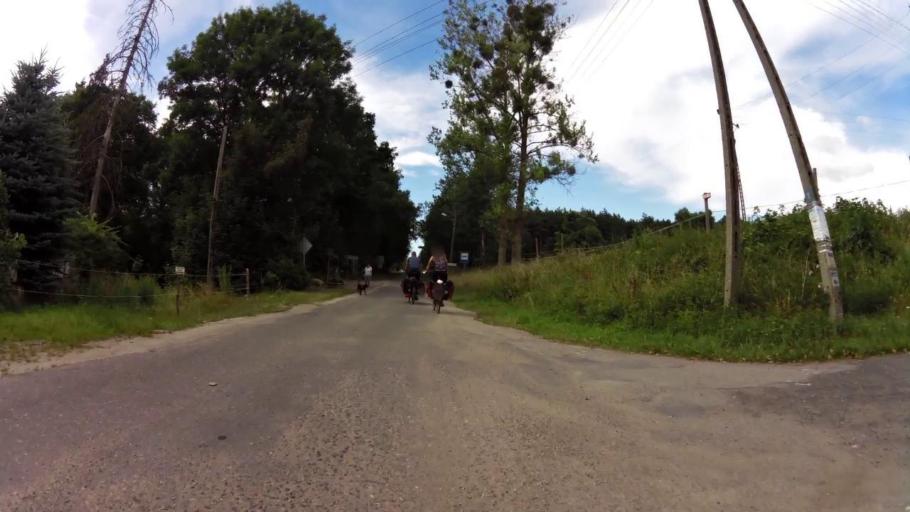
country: PL
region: West Pomeranian Voivodeship
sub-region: Powiat lobeski
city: Lobez
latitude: 53.6023
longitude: 15.6617
